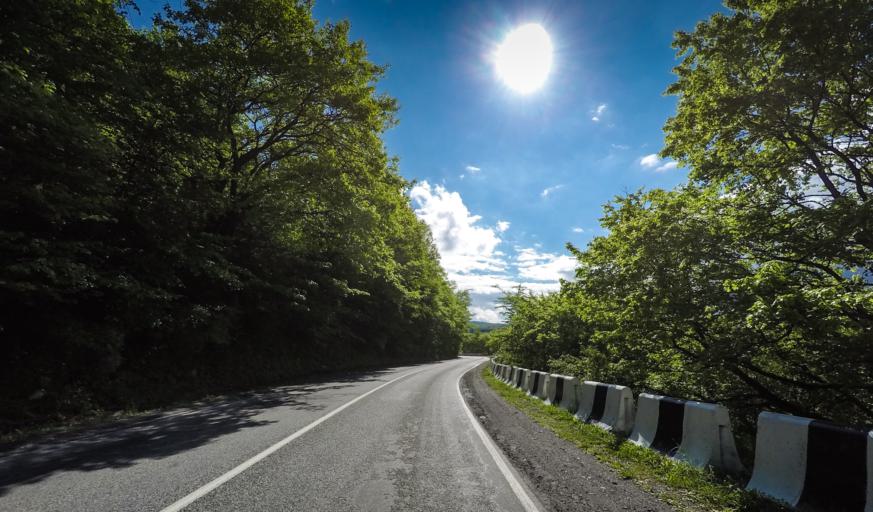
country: RU
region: North Ossetia
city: Vladikavkaz
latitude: 42.9374
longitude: 44.6481
